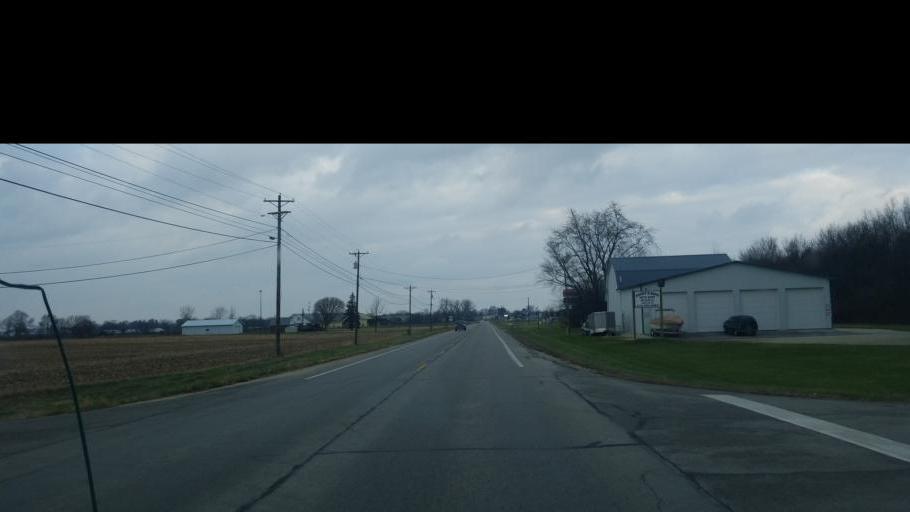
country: US
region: Ohio
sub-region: Mercer County
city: Celina
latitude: 40.5273
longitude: -84.5772
